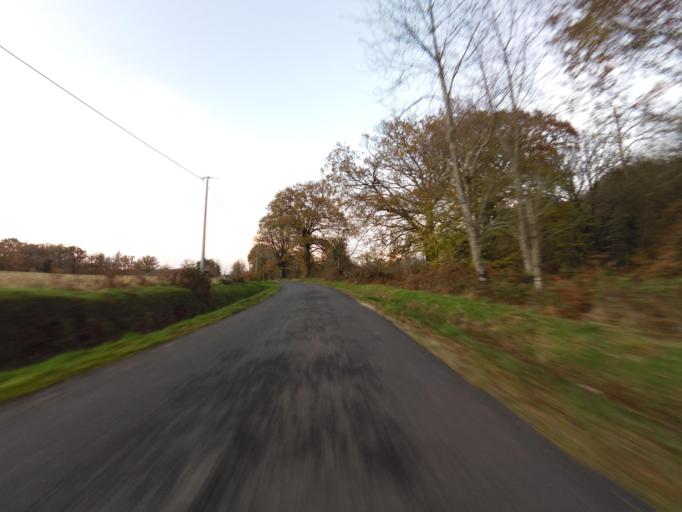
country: FR
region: Brittany
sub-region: Departement du Morbihan
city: Pluherlin
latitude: 47.7202
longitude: -2.3648
